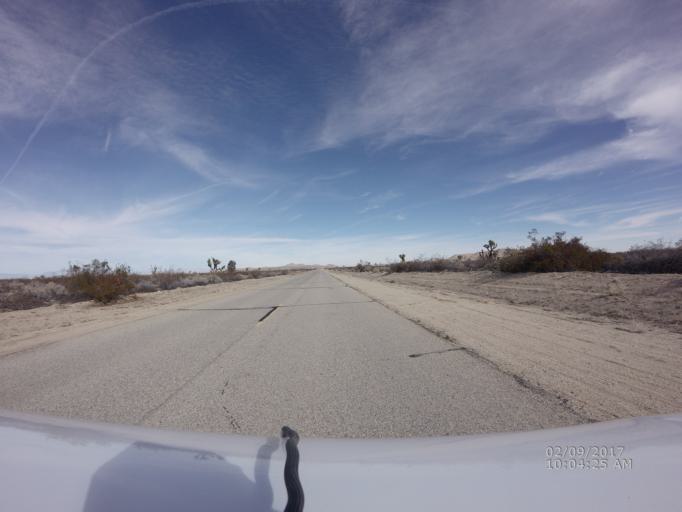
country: US
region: California
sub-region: Los Angeles County
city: Lake Los Angeles
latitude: 34.5611
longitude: -117.8896
